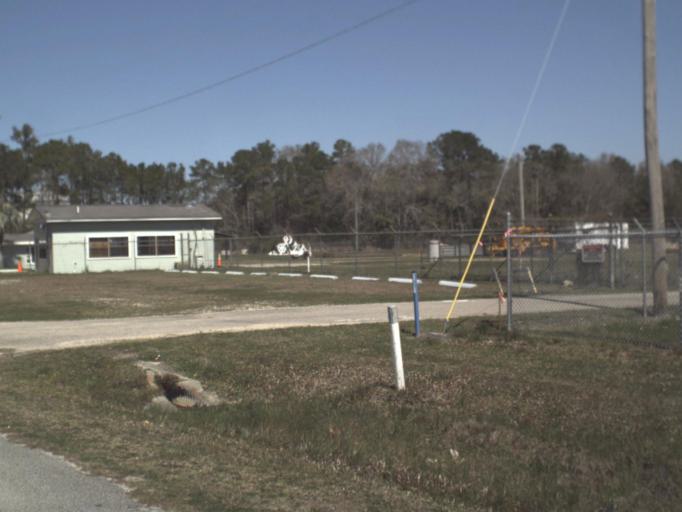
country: US
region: Florida
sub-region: Leon County
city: Woodville
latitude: 30.1639
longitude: -84.2071
